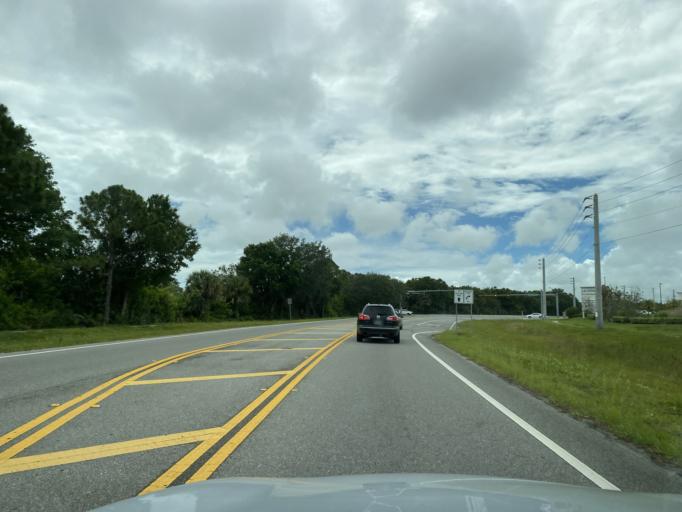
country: US
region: Florida
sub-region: Brevard County
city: West Melbourne
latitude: 28.0383
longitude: -80.6509
